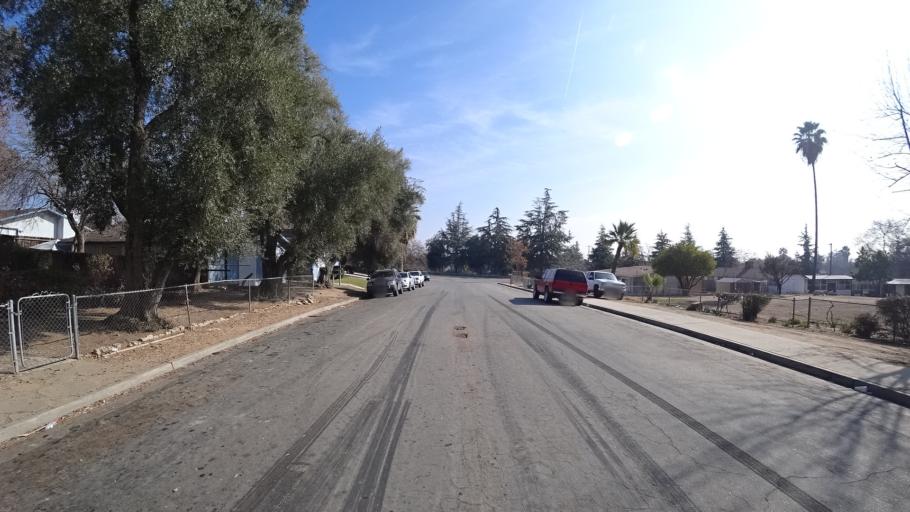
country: US
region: California
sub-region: Kern County
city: Bakersfield
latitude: 35.3885
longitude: -118.9845
